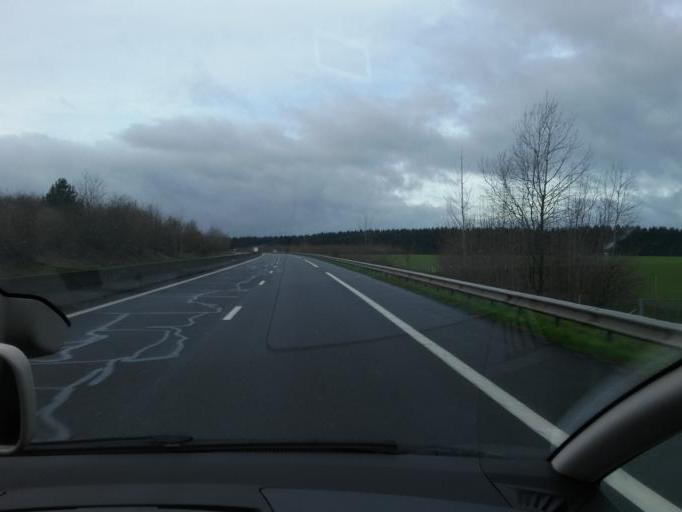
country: FR
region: Picardie
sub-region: Departement de la Somme
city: Villers-Bretonneux
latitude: 49.8592
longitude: 2.4795
